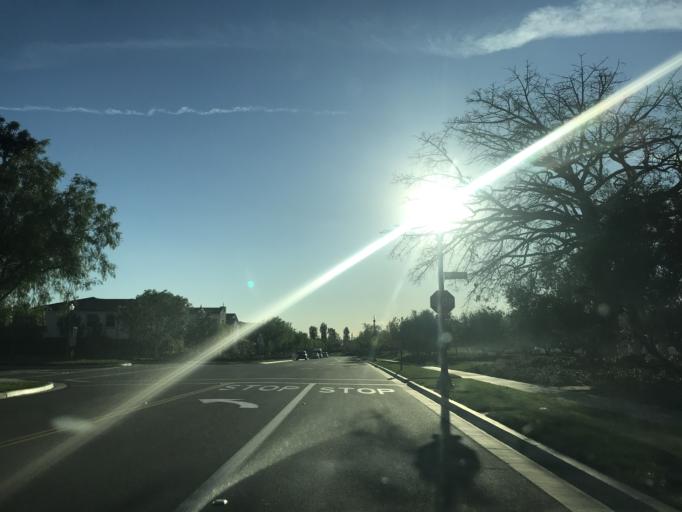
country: US
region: California
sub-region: Orange County
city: North Tustin
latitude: 33.7154
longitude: -117.7481
